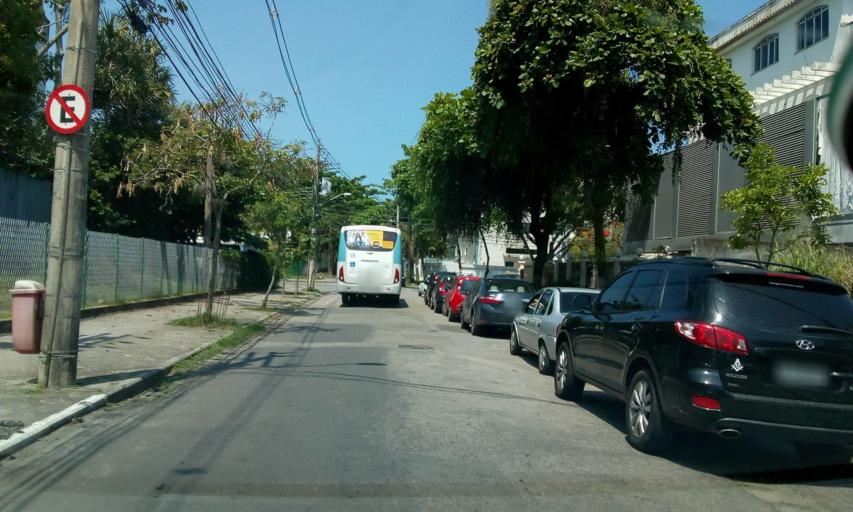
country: BR
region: Rio de Janeiro
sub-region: Nilopolis
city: Nilopolis
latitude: -23.0203
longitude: -43.4813
